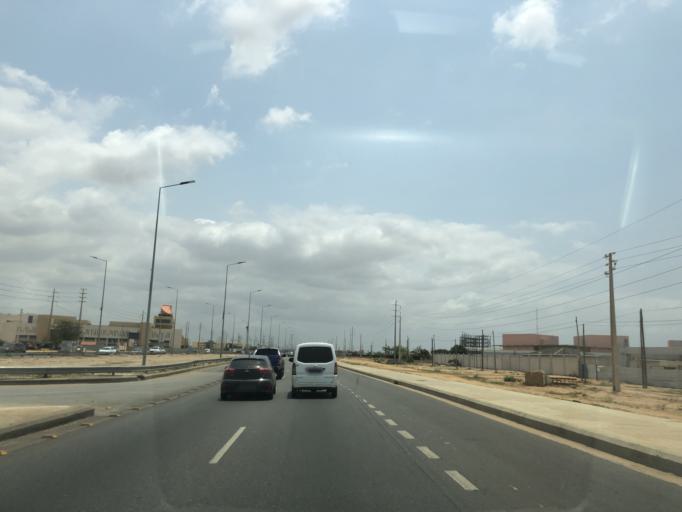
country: AO
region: Luanda
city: Luanda
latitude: -8.9580
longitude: 13.2574
